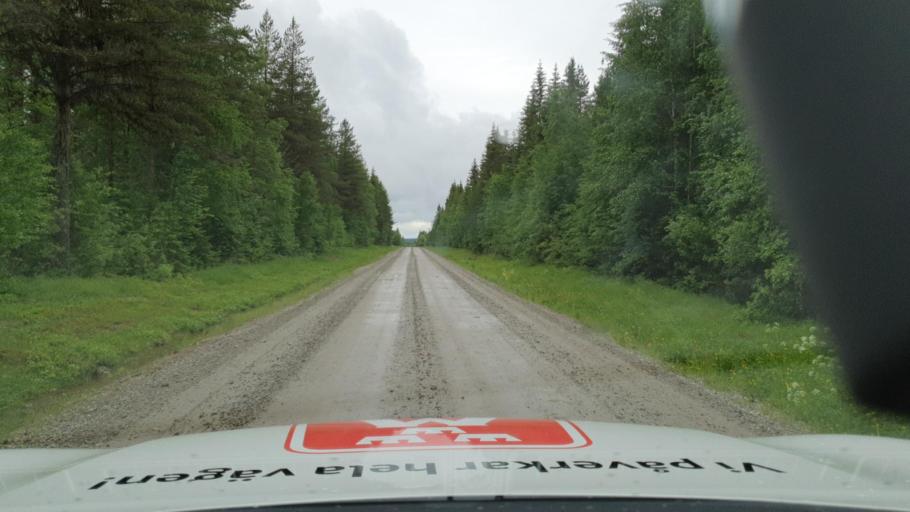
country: SE
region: Vaesterbotten
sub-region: Dorotea Kommun
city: Dorotea
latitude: 64.0805
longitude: 16.6870
